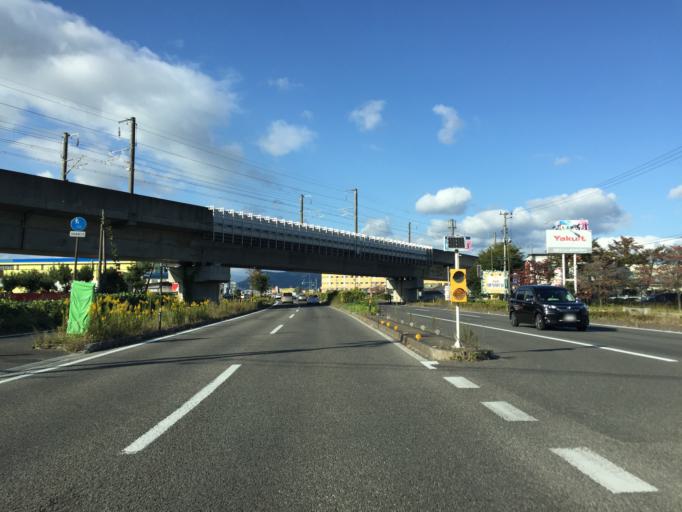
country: JP
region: Fukushima
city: Fukushima-shi
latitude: 37.7783
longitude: 140.4652
